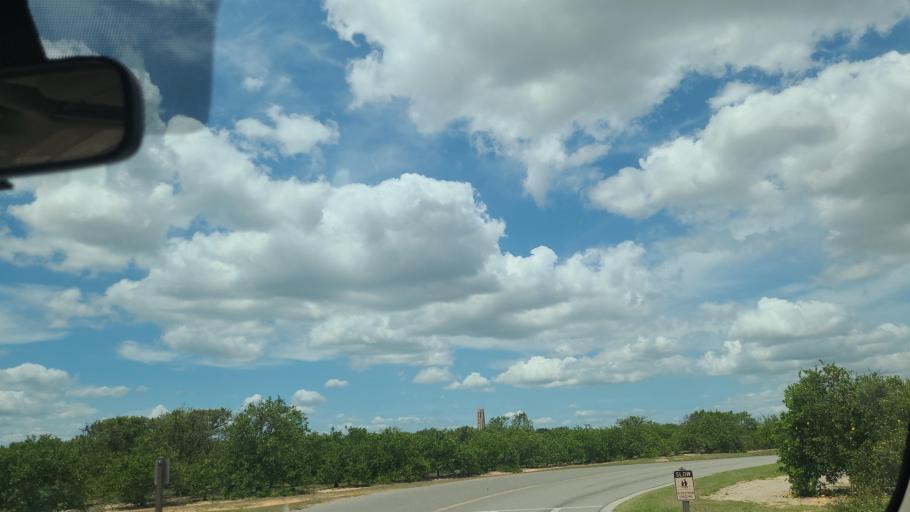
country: US
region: Florida
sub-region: Polk County
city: Lake Wales
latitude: 27.9267
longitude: -81.5694
